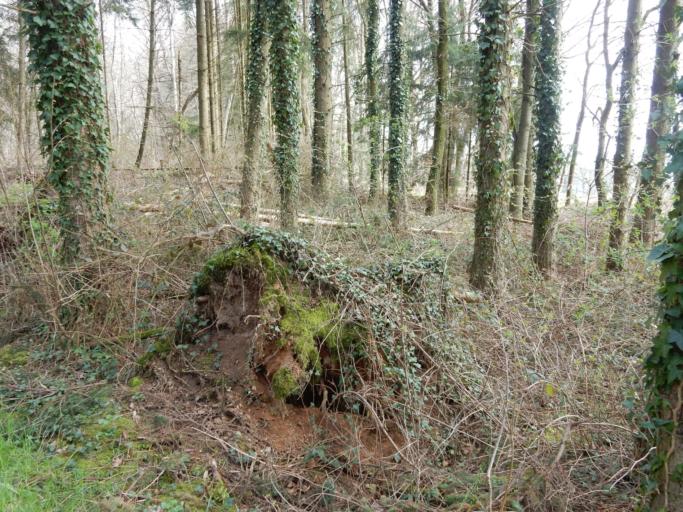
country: DE
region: Rheinland-Pfalz
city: Gentingen
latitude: 49.8820
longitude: 6.2484
